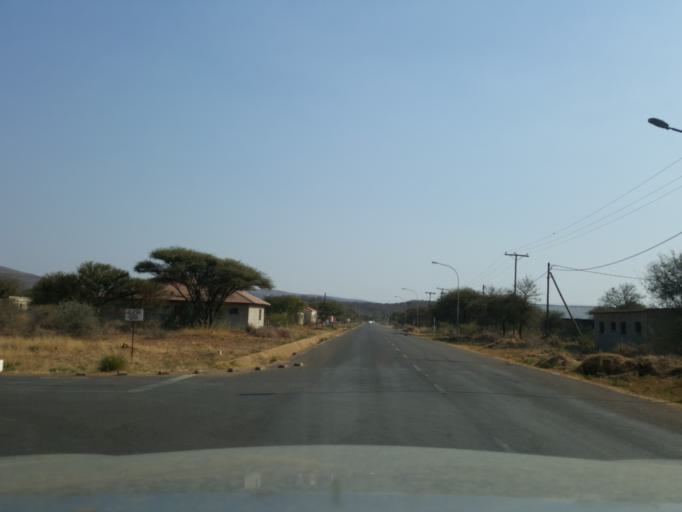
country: BW
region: South East
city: Lobatse
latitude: -25.1923
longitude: 25.6949
